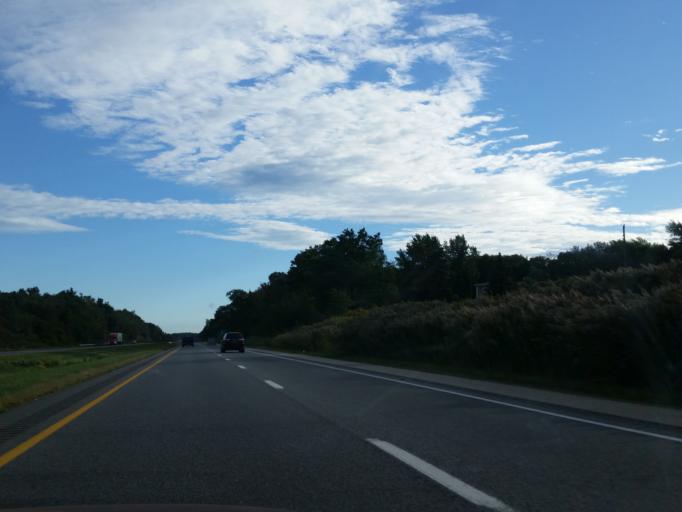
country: US
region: Pennsylvania
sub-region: Erie County
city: North East
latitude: 42.2073
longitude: -79.8067
